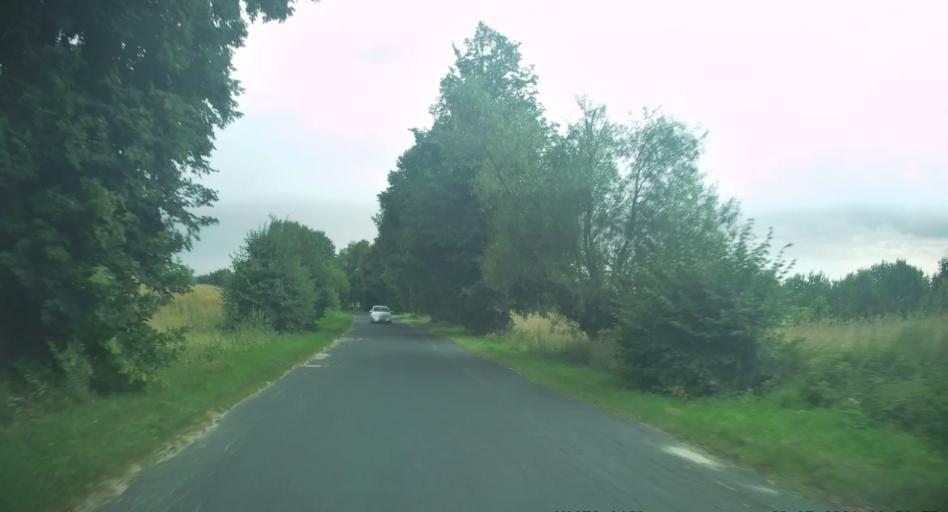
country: PL
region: Lodz Voivodeship
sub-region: Powiat rawski
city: Rawa Mazowiecka
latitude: 51.7589
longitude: 20.1869
